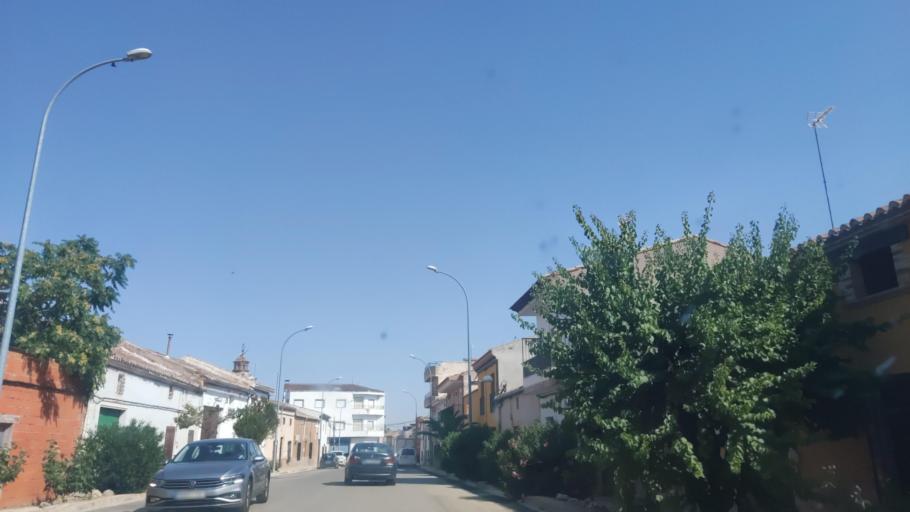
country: ES
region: Castille-La Mancha
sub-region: Provincia de Albacete
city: La Gineta
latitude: 39.1120
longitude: -1.9953
